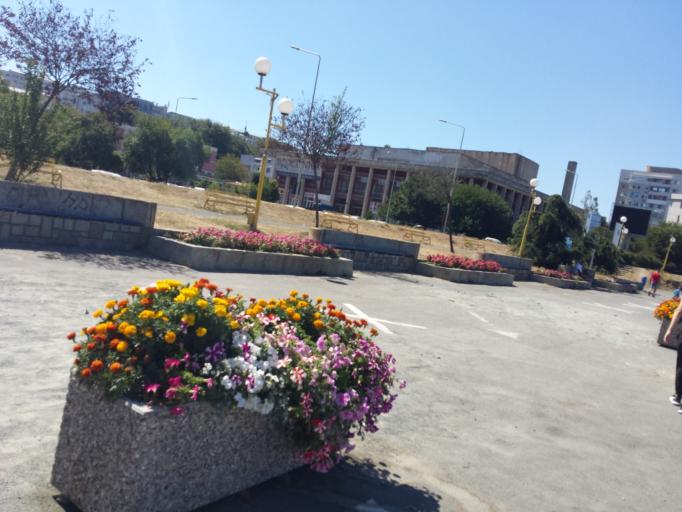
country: RO
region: Tulcea
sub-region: Municipiul Tulcea
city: Tulcea
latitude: 45.1802
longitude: 28.7975
